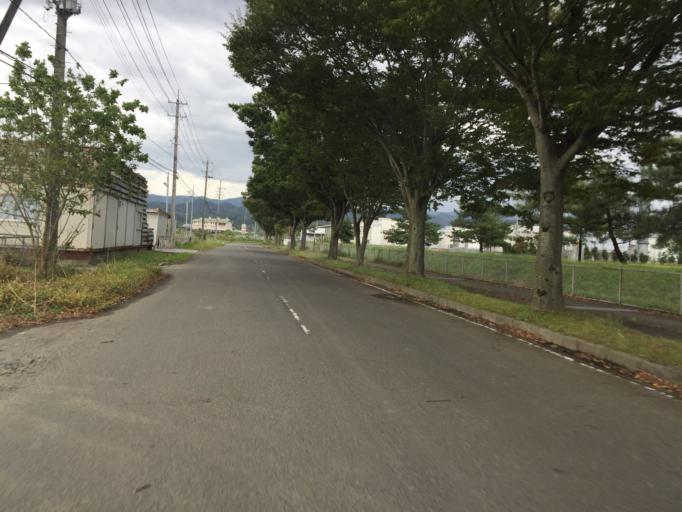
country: JP
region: Fukushima
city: Yanagawamachi-saiwaicho
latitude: 37.8612
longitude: 140.5945
